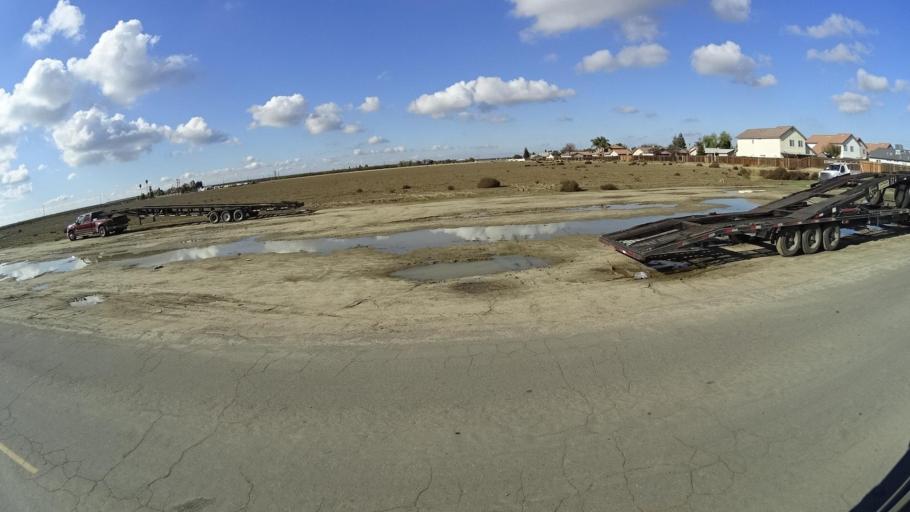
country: US
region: California
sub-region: Kern County
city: McFarland
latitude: 35.6630
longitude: -119.2321
